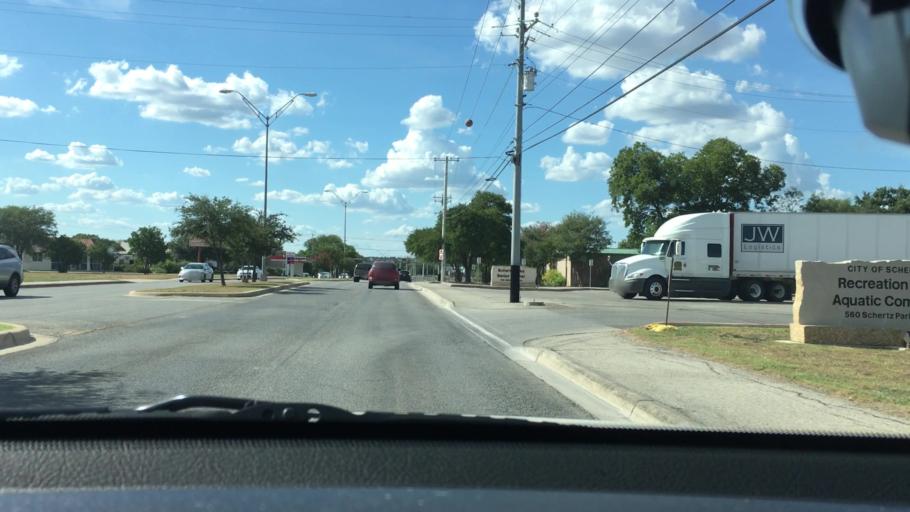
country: US
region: Texas
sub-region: Guadalupe County
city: Schertz
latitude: 29.5591
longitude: -98.2662
